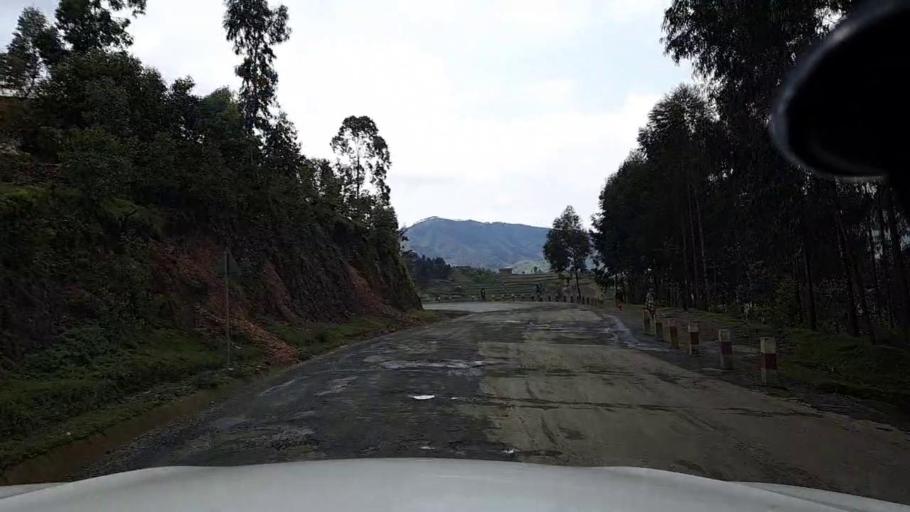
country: RW
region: Western Province
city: Kibuye
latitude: -2.0583
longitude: 29.5239
